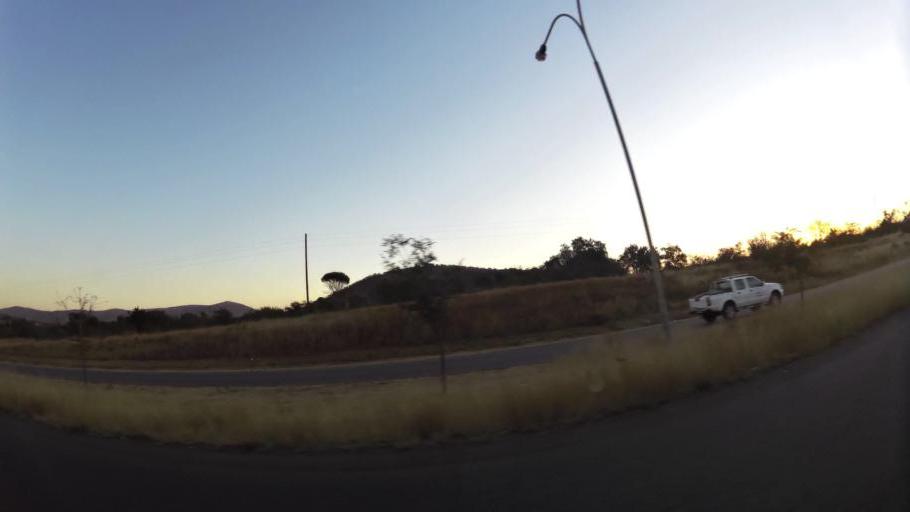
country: ZA
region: North-West
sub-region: Bojanala Platinum District Municipality
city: Rustenburg
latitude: -25.6252
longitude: 27.1855
